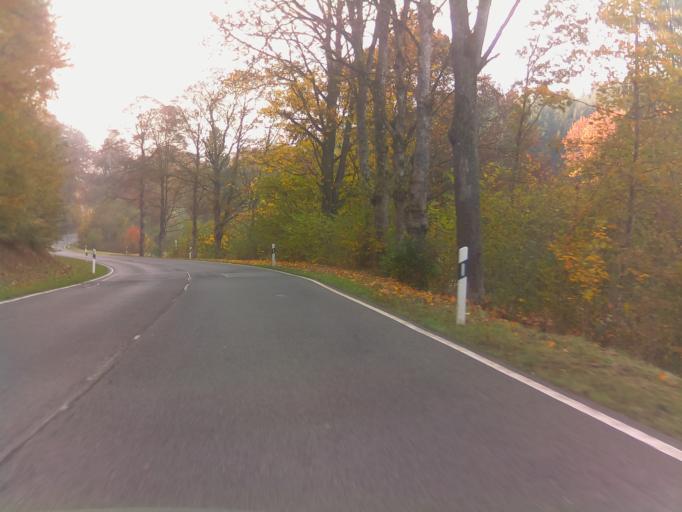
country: DE
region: Baden-Wuerttemberg
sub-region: Karlsruhe Region
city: Epfenbach
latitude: 49.3691
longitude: 8.9120
